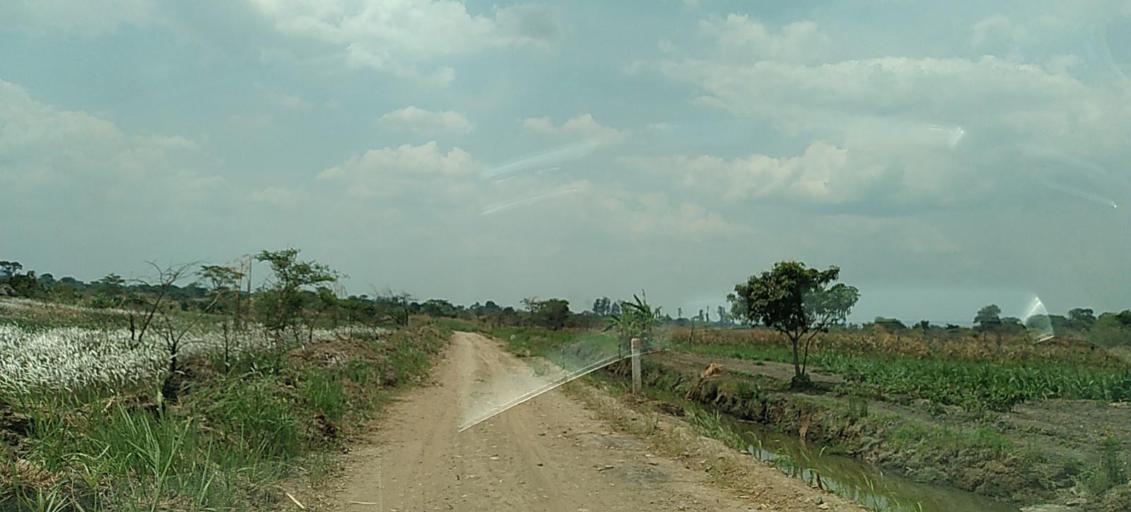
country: ZM
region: Copperbelt
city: Chililabombwe
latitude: -12.3723
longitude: 27.8003
